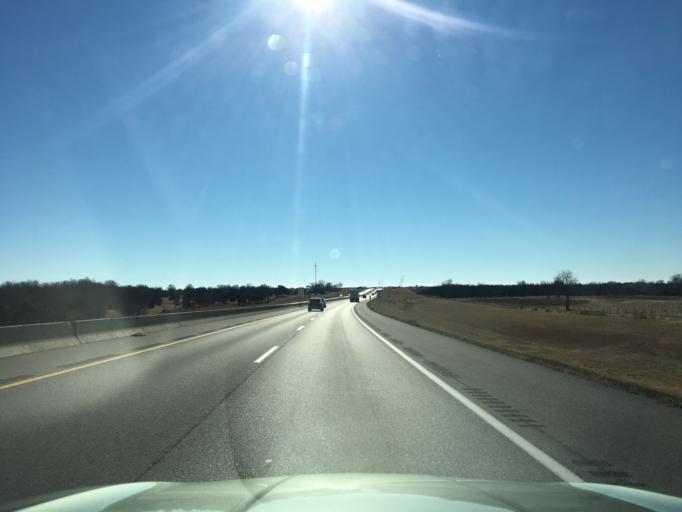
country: US
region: Kansas
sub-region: Sumner County
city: Wellington
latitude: 37.2605
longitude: -97.3392
